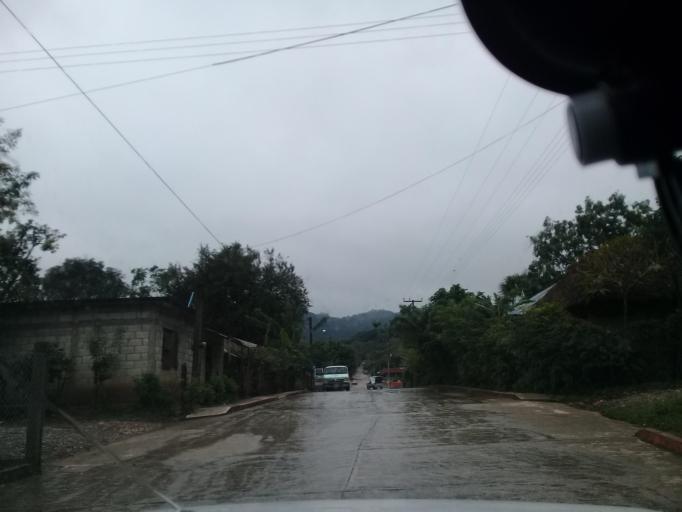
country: MX
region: Veracruz
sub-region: Chalma
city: San Pedro Coyutla
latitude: 21.2247
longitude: -98.4287
